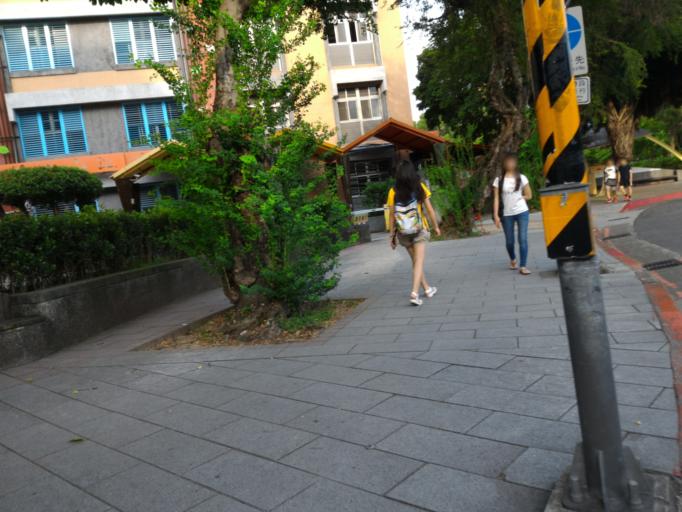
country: TW
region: Taipei
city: Taipei
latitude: 25.0356
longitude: 121.5151
